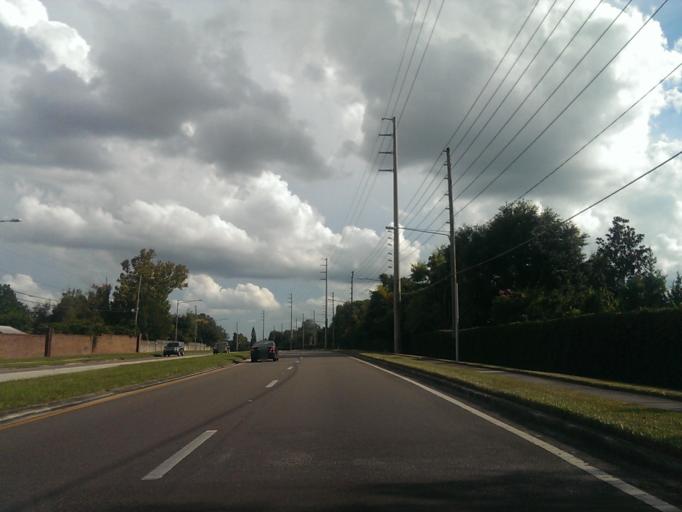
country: US
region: Florida
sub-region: Orange County
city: Bay Hill
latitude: 28.4754
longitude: -81.5083
